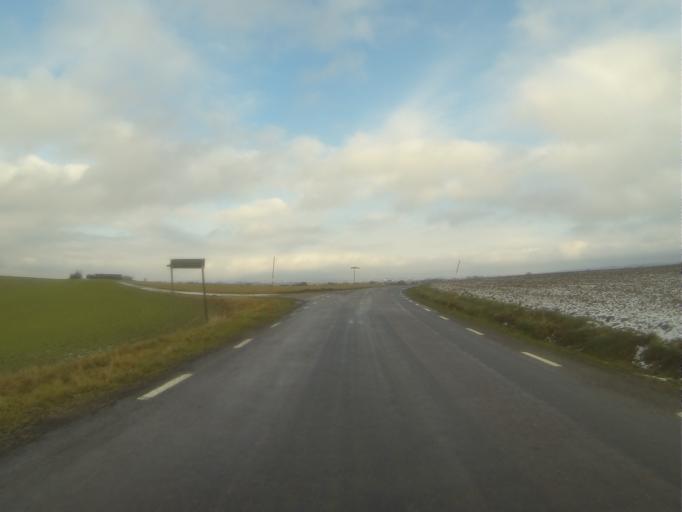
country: SE
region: Skane
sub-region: Svedala Kommun
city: Klagerup
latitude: 55.5903
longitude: 13.2931
